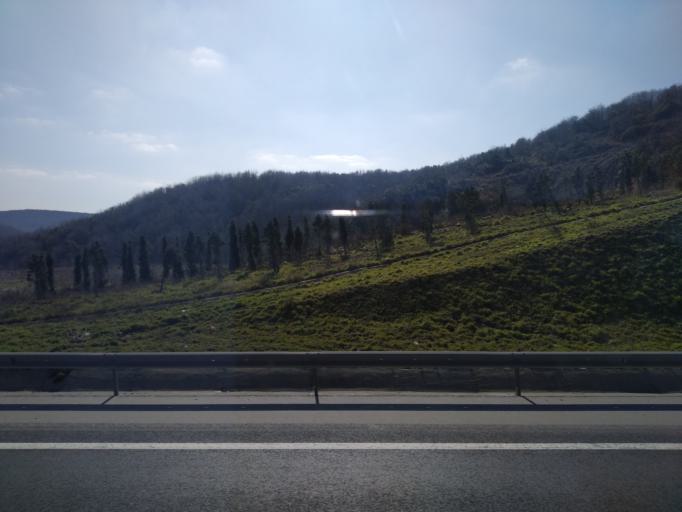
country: TR
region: Istanbul
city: Arikoey
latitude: 41.2329
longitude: 28.9630
